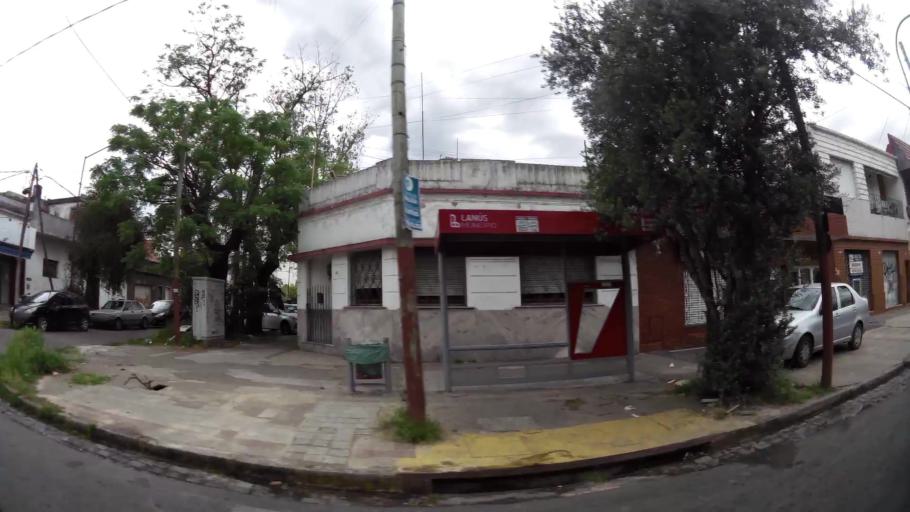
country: AR
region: Buenos Aires
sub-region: Partido de Lanus
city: Lanus
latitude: -34.6955
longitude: -58.3953
